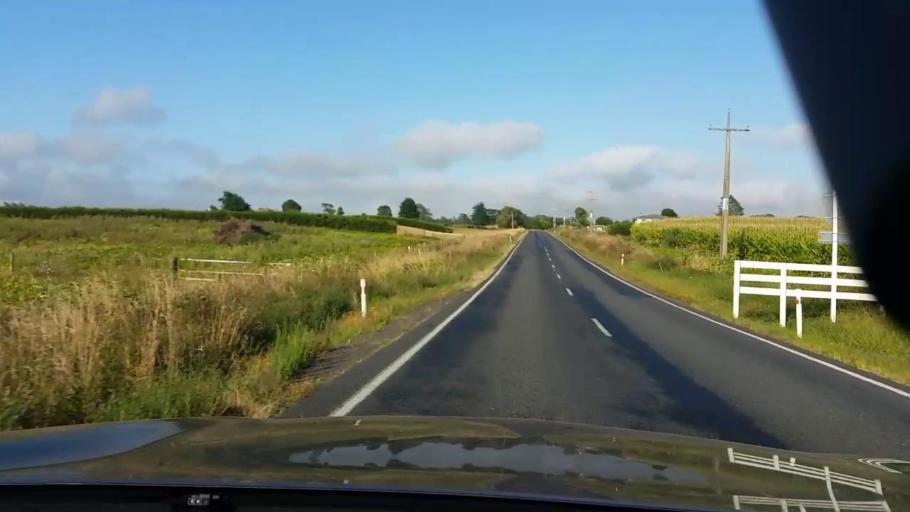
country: NZ
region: Waikato
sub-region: Hamilton City
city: Hamilton
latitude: -37.5905
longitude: 175.3868
